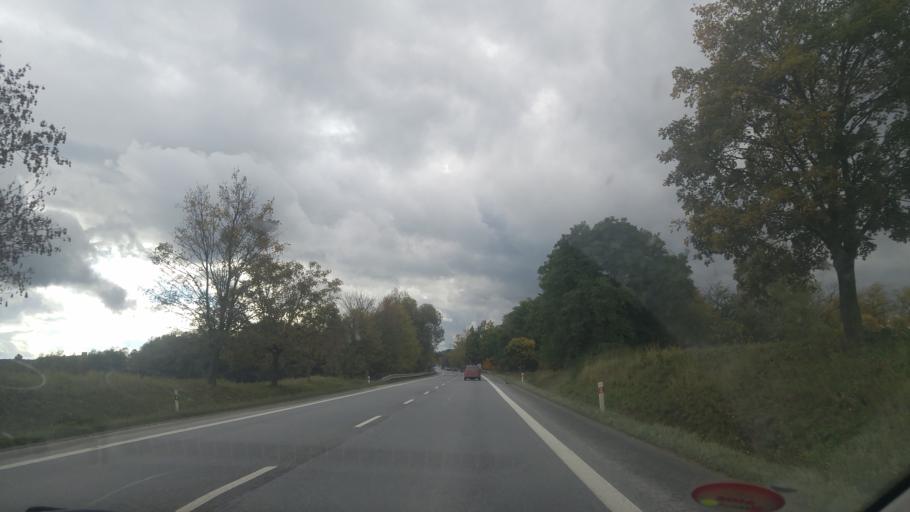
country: CZ
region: Jihocesky
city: Sevetin
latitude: 49.1211
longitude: 14.5947
